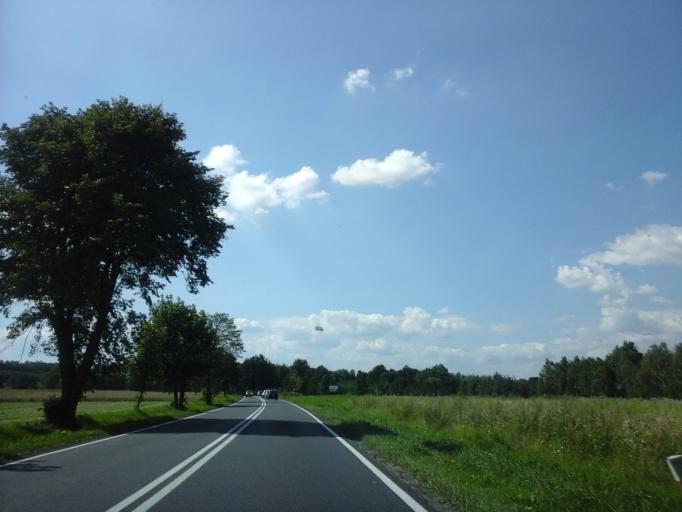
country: PL
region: Lesser Poland Voivodeship
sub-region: Powiat oswiecimski
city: Przeciszow
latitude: 50.0153
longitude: 19.3554
